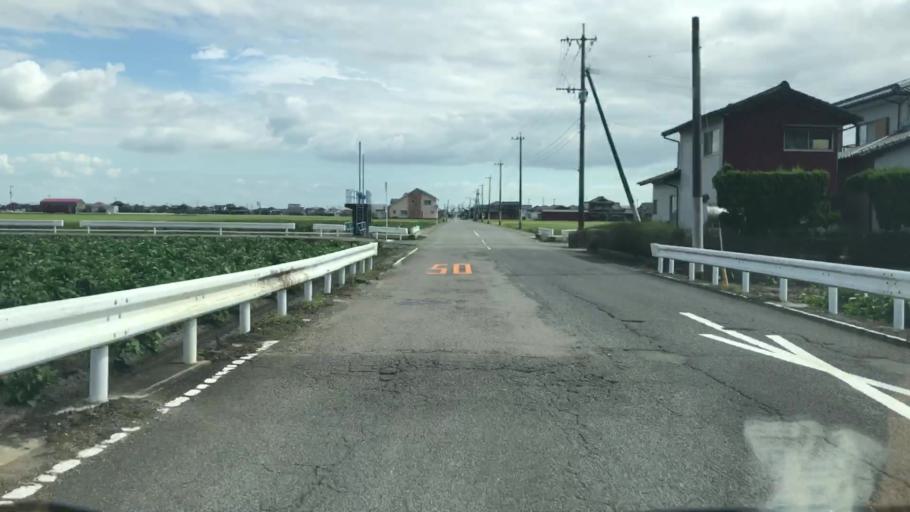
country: JP
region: Saga Prefecture
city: Saga-shi
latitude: 33.2237
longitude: 130.1764
